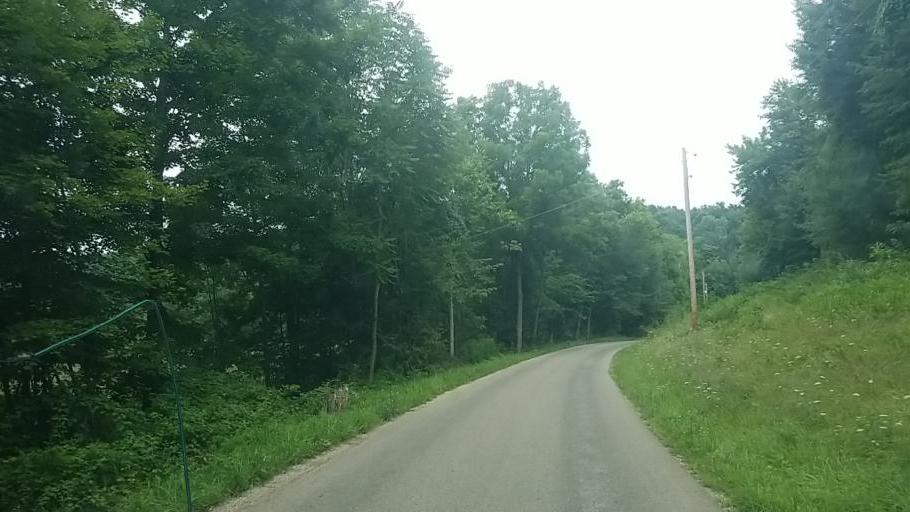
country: US
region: Ohio
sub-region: Licking County
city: Utica
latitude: 40.2464
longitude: -82.2876
